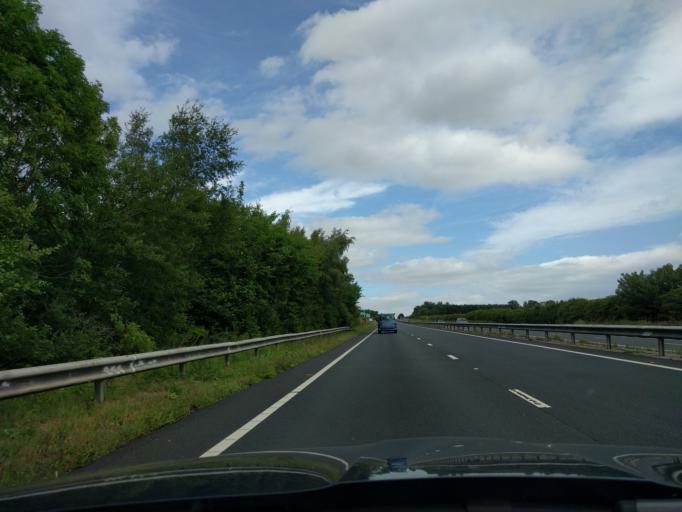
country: GB
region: England
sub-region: Northumberland
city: Felton
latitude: 55.3097
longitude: -1.7257
